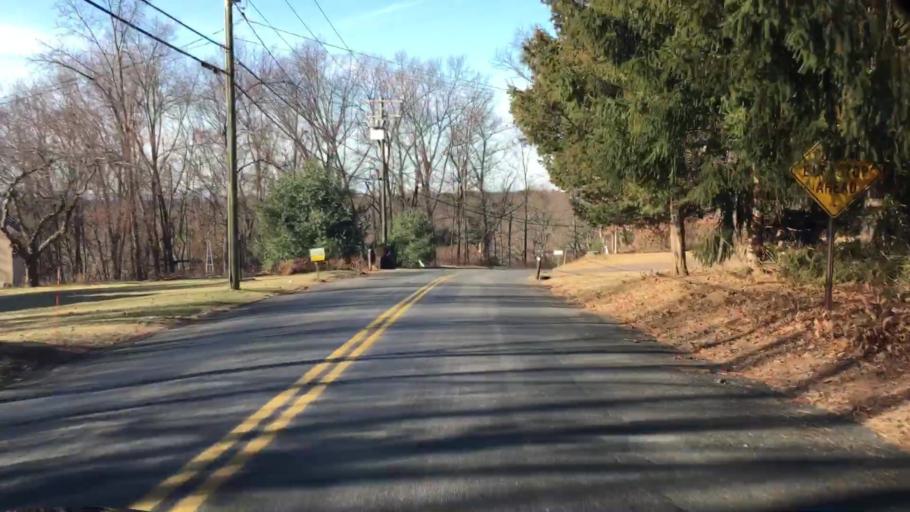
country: US
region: Connecticut
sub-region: Tolland County
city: Somers
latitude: 41.9714
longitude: -72.4414
